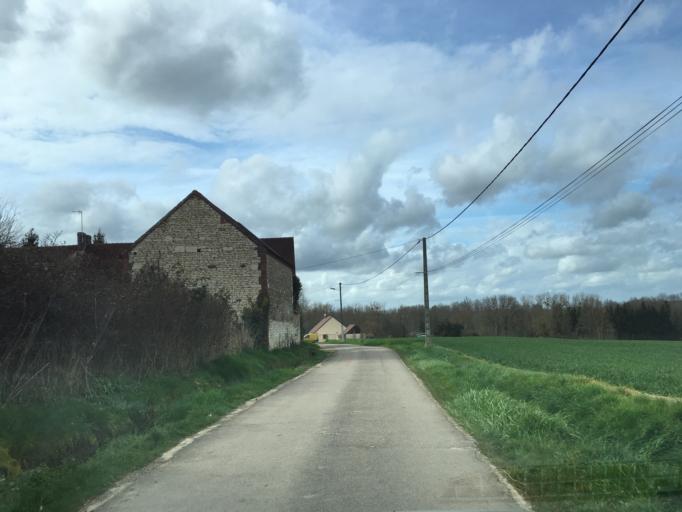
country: FR
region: Bourgogne
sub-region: Departement de l'Yonne
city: Fleury-la-Vallee
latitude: 47.8630
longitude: 3.4095
